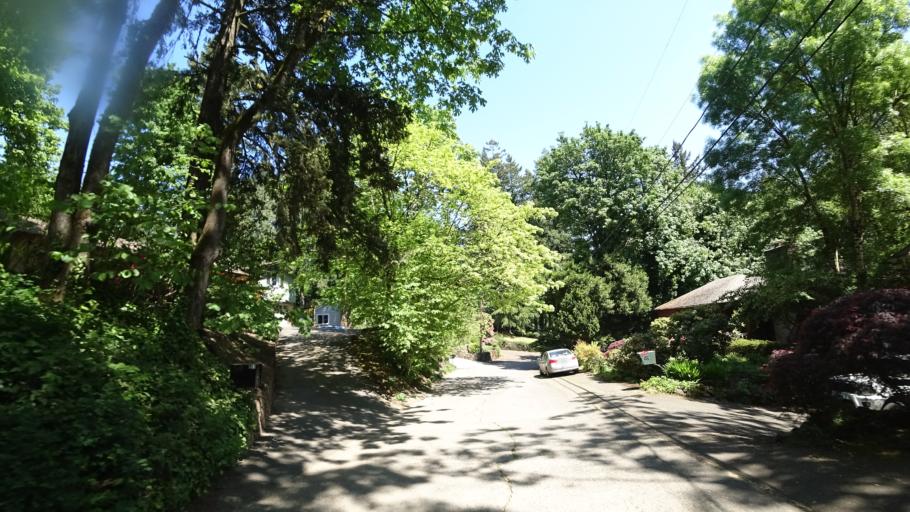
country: US
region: Oregon
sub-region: Multnomah County
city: Portland
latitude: 45.4810
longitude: -122.6894
